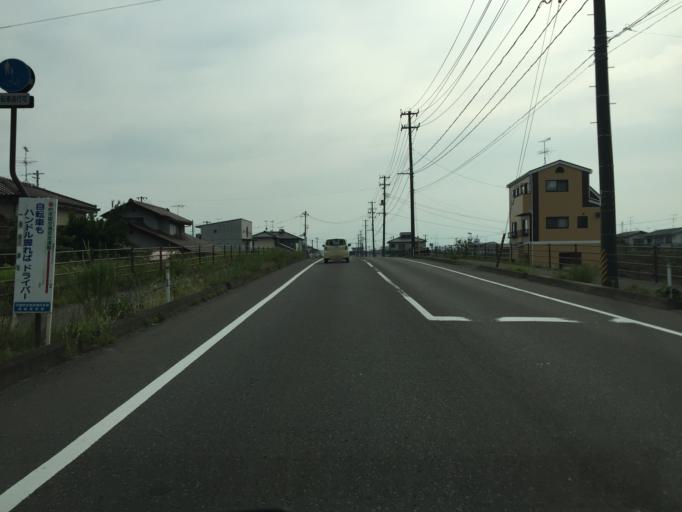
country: JP
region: Fukushima
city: Fukushima-shi
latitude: 37.7518
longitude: 140.4848
